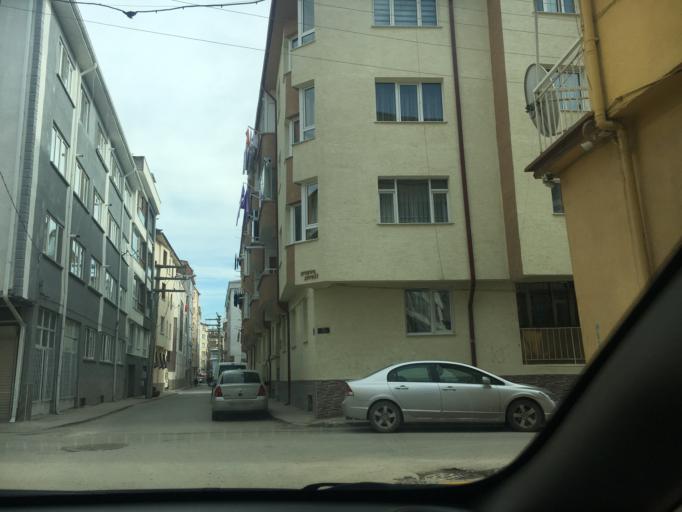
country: TR
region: Eskisehir
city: Eskisehir
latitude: 39.7726
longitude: 30.5068
